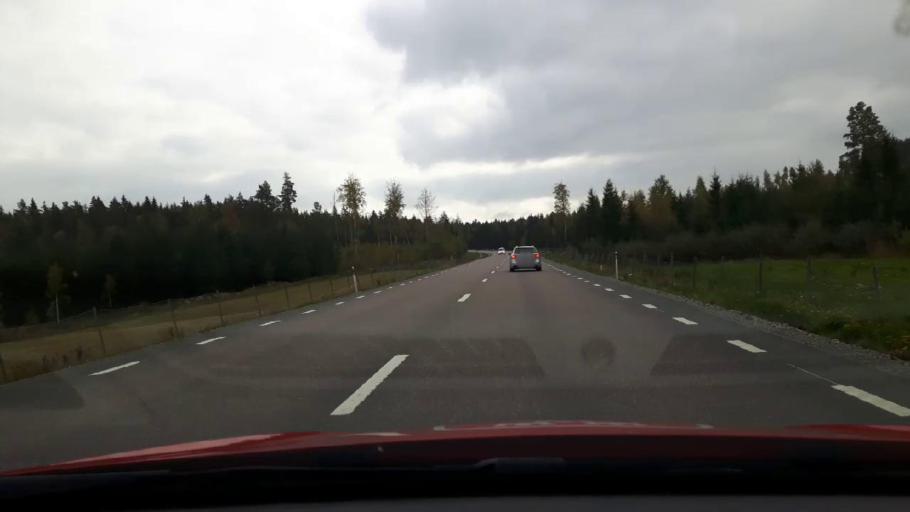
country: SE
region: Gaevleborg
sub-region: Bollnas Kommun
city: Bollnas
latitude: 61.3035
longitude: 16.4675
